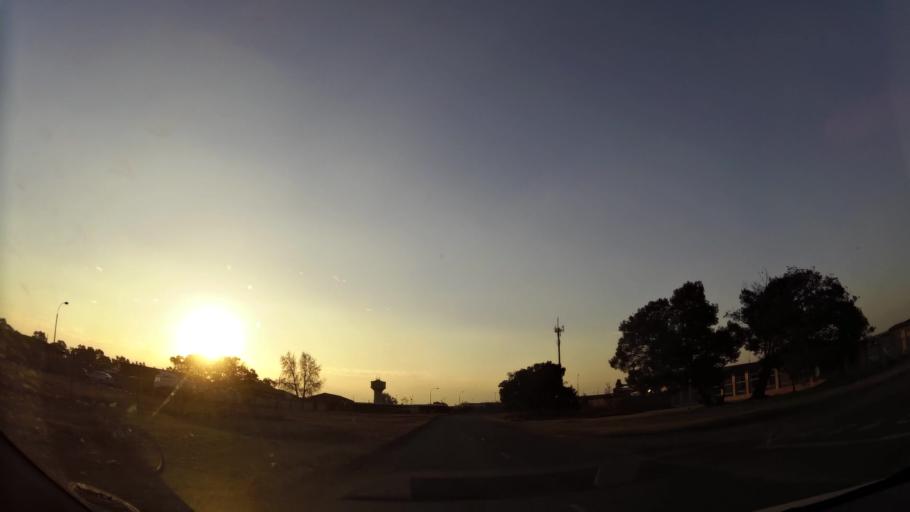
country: ZA
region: Gauteng
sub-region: West Rand District Municipality
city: Randfontein
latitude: -26.2051
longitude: 27.7039
